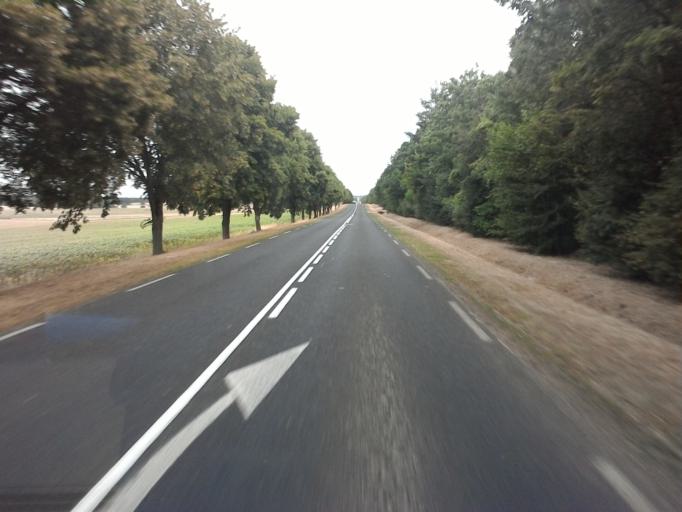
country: FR
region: Lorraine
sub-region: Departement de Meurthe-et-Moselle
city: Colombey-les-Belles
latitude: 48.5018
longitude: 5.8752
